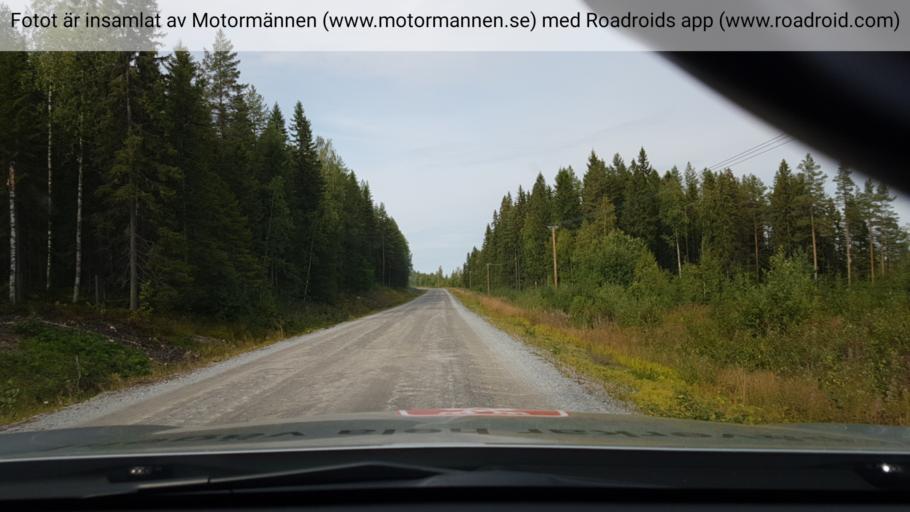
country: SE
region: Vaesterbotten
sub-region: Bjurholms Kommun
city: Bjurholm
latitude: 63.8935
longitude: 19.4160
